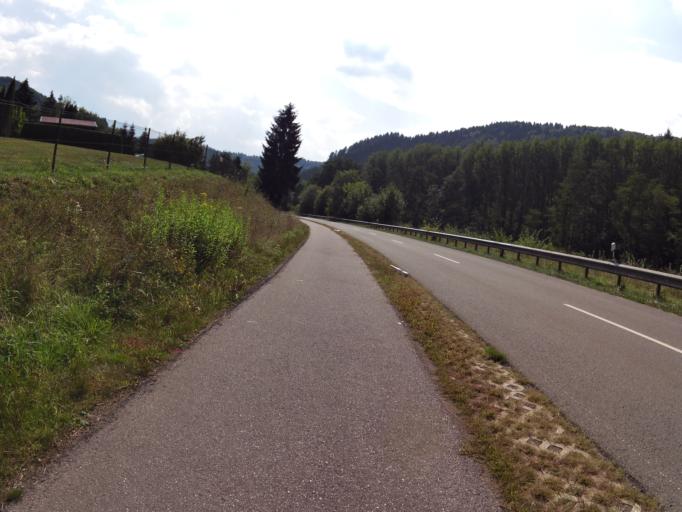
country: DE
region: Rheinland-Pfalz
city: Orenhofen
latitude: 49.8688
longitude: 6.6421
